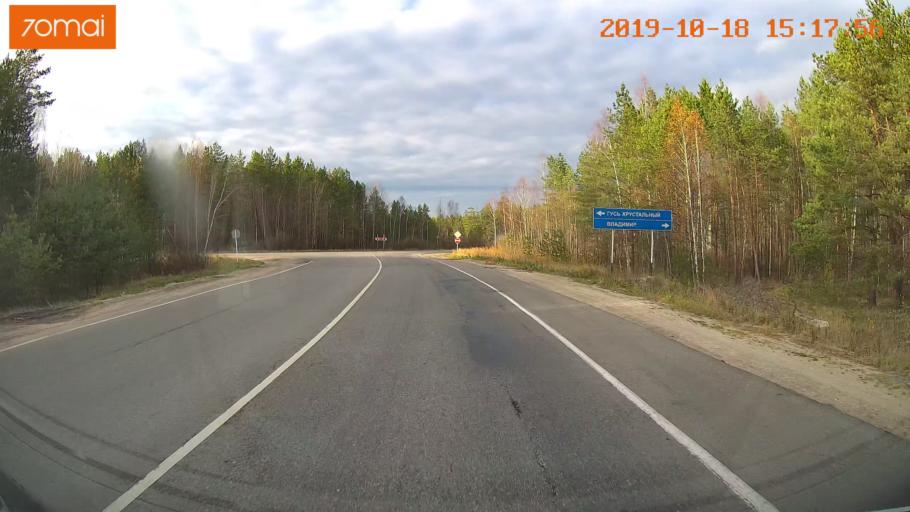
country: RU
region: Vladimir
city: Anopino
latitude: 55.6565
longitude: 40.7271
